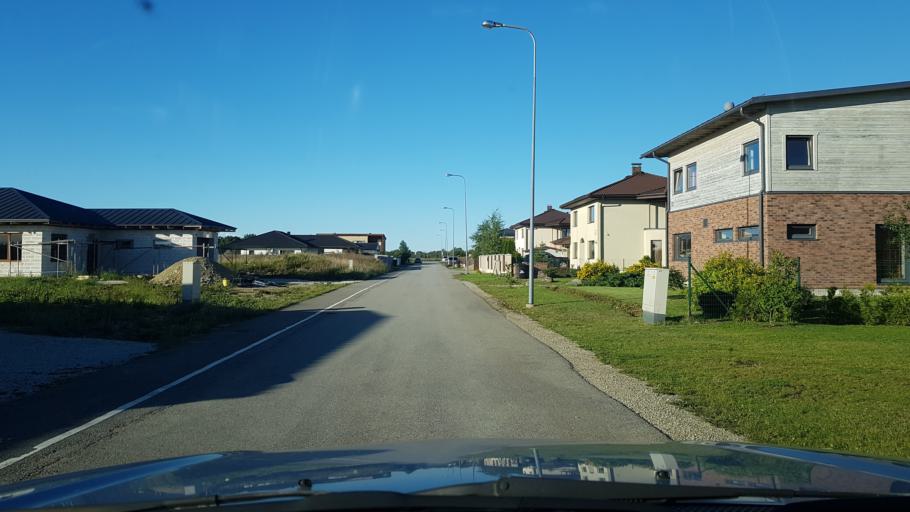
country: EE
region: Harju
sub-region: Rae vald
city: Jueri
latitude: 59.3842
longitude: 24.8437
